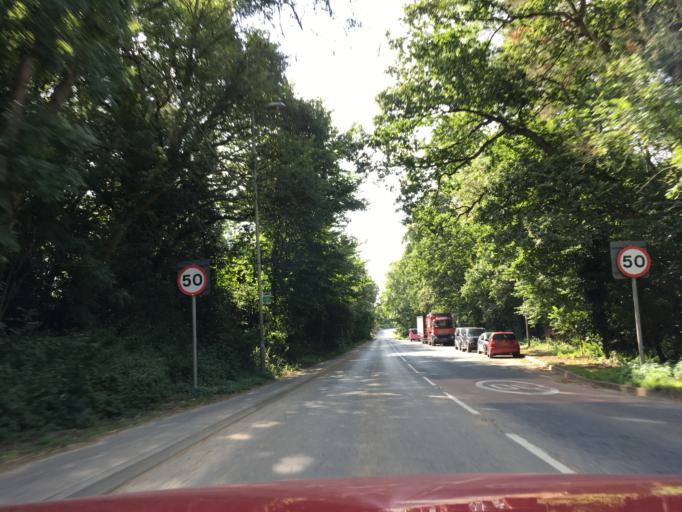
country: GB
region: England
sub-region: Hampshire
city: Bishops Waltham
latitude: 50.9503
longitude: -1.2080
